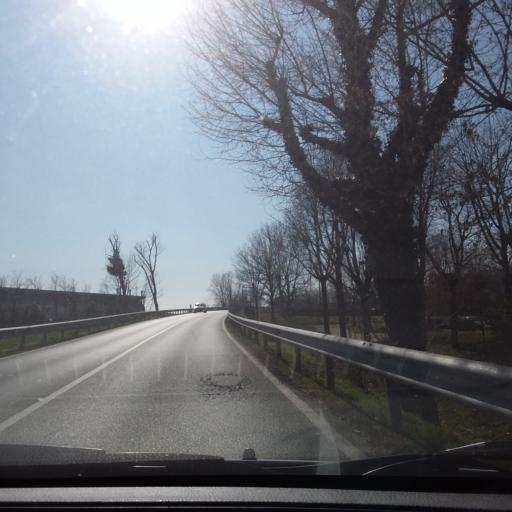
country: IT
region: Piedmont
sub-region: Provincia di Torino
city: Rivoli
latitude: 45.0630
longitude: 7.5291
